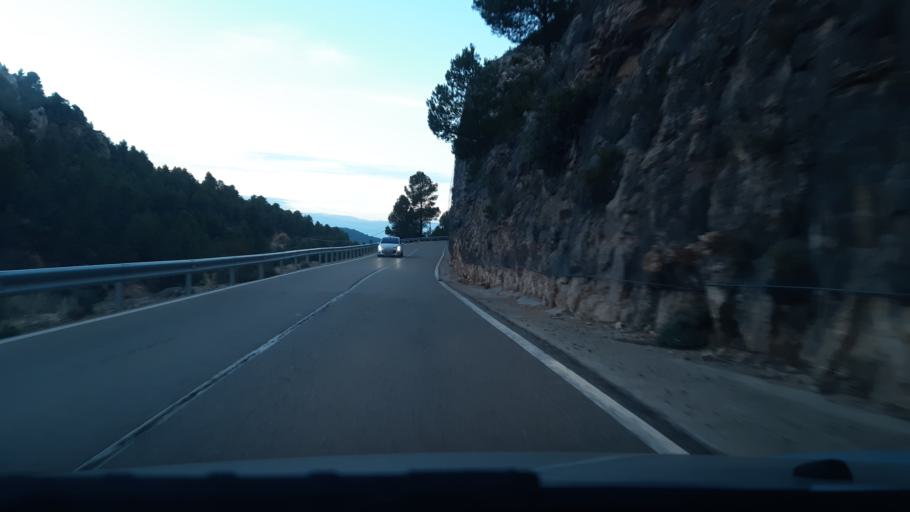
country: ES
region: Aragon
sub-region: Provincia de Teruel
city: Valderrobres
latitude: 40.8437
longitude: 0.1756
